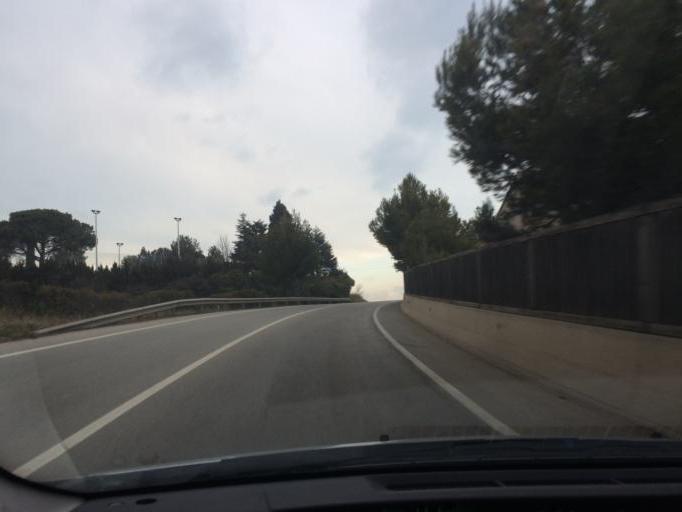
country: ES
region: Catalonia
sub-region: Provincia de Barcelona
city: Manresa
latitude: 41.7464
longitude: 1.8403
